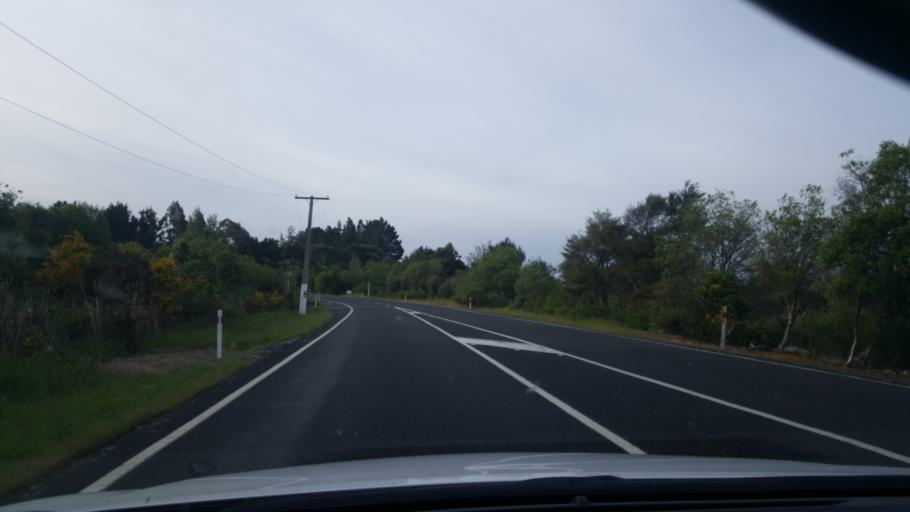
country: NZ
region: Waikato
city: Turangi
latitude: -38.9622
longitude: 175.7651
